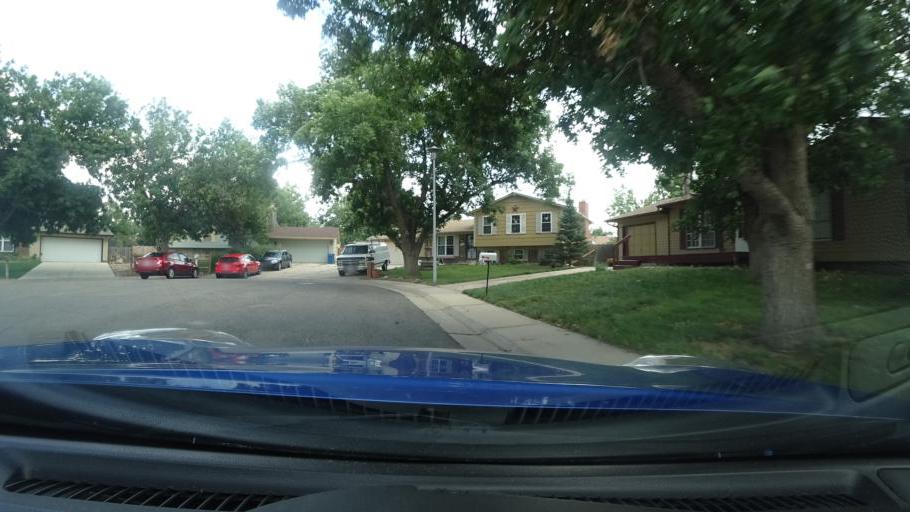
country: US
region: Colorado
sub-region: Adams County
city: Aurora
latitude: 39.6914
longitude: -104.7844
